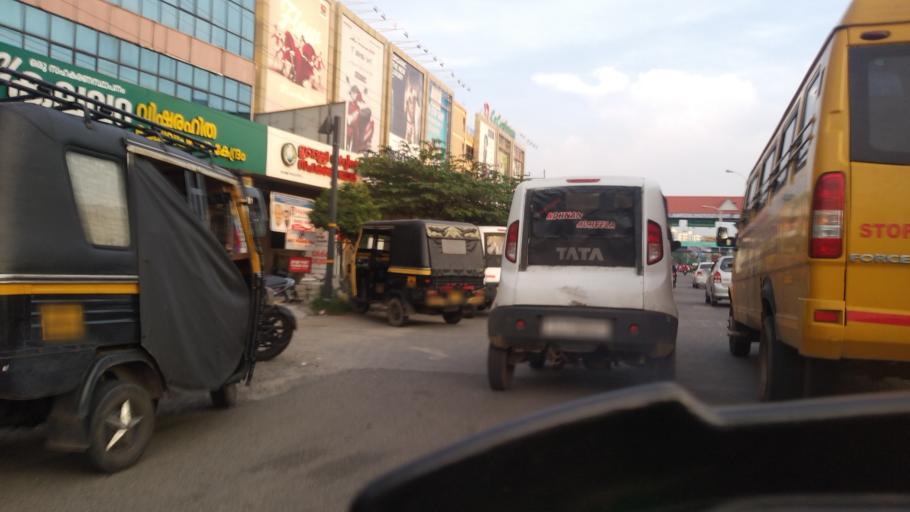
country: IN
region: Kerala
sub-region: Ernakulam
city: Elur
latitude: 10.0262
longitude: 76.3066
